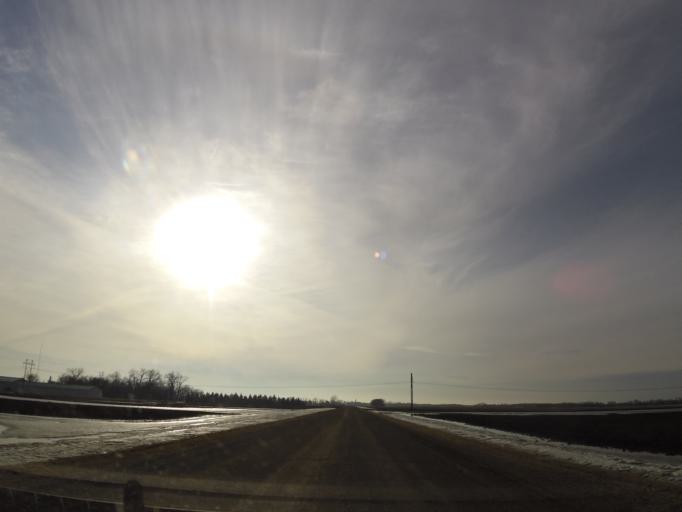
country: US
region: North Dakota
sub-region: Walsh County
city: Grafton
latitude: 48.4266
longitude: -97.2633
